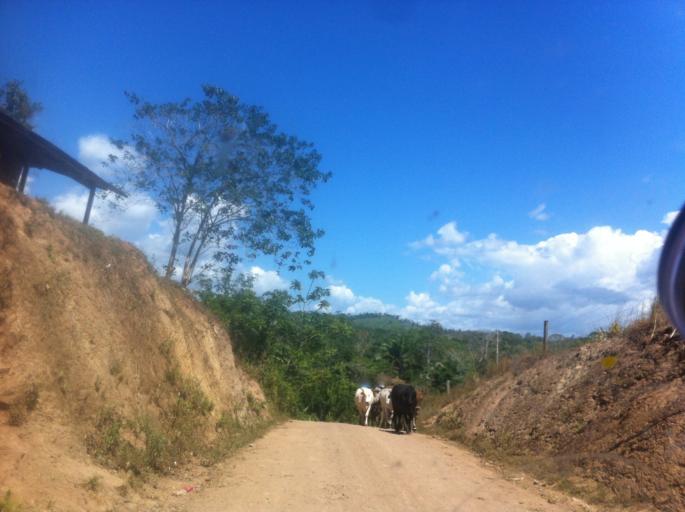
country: CR
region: Alajuela
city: Los Chiles
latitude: 11.2493
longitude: -84.4469
